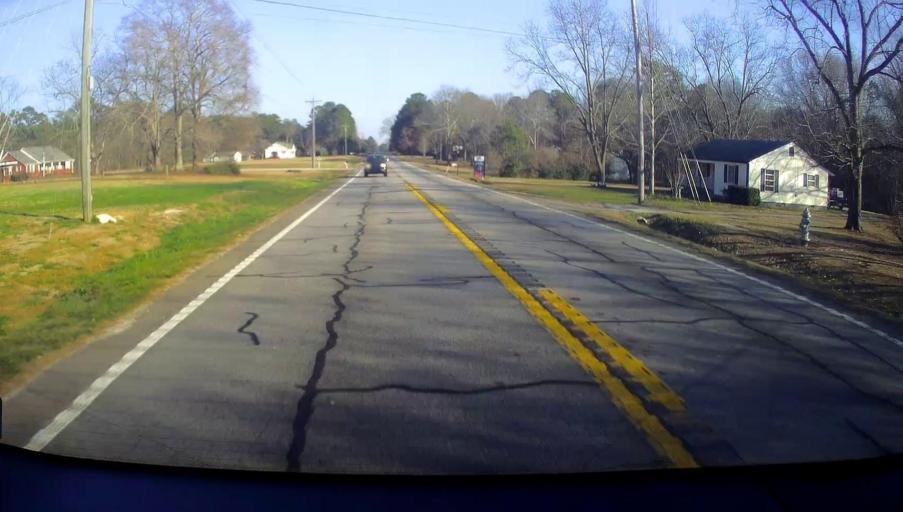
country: US
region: Georgia
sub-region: Henry County
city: Hampton
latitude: 33.4241
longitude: -84.2756
